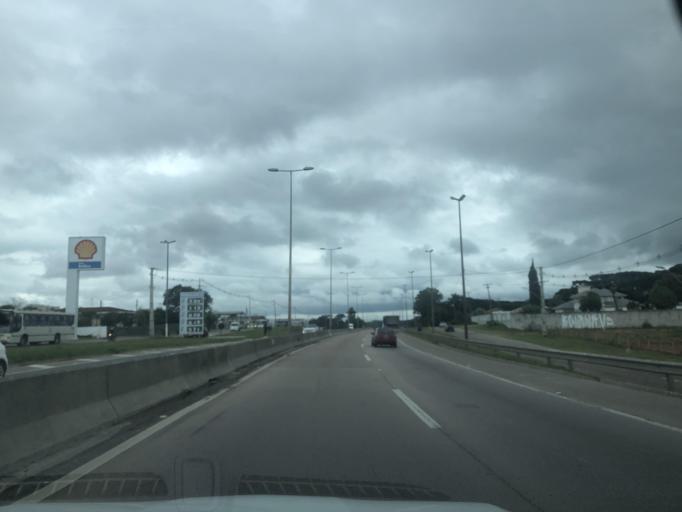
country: BR
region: Parana
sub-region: Araucaria
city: Araucaria
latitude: -25.6568
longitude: -49.3121
